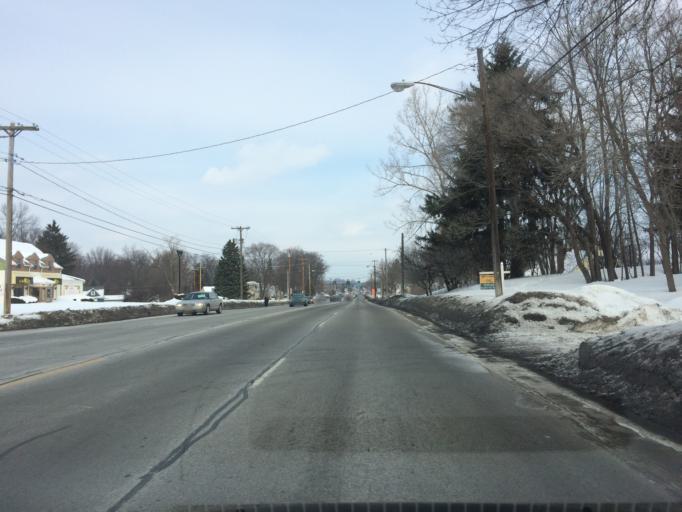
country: US
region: New York
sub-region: Monroe County
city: Rochester
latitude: 43.1072
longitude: -77.6262
